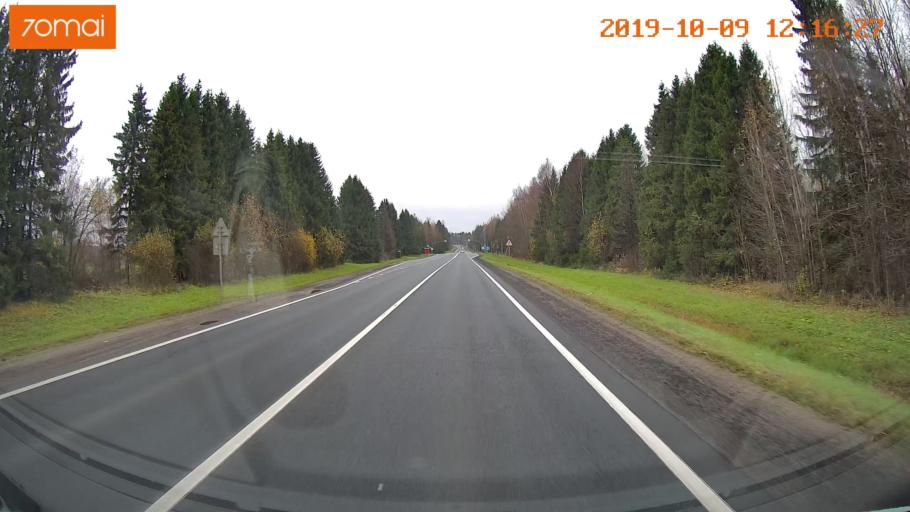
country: RU
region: Jaroslavl
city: Prechistoye
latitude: 58.4684
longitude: 40.3211
